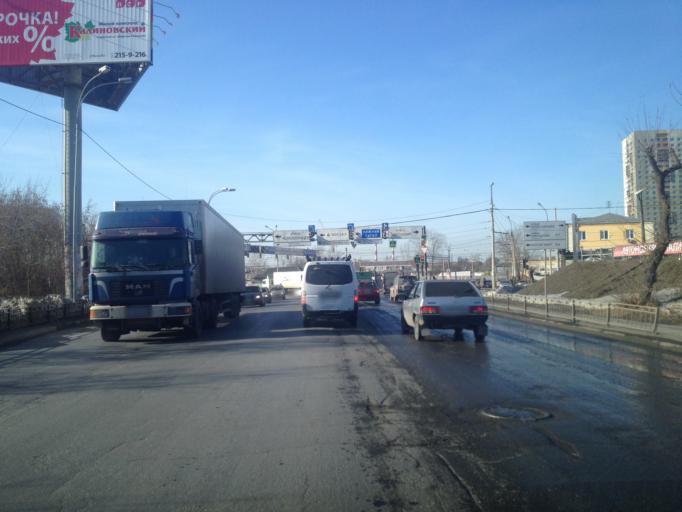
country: RU
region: Sverdlovsk
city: Yekaterinburg
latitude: 56.8567
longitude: 60.6159
